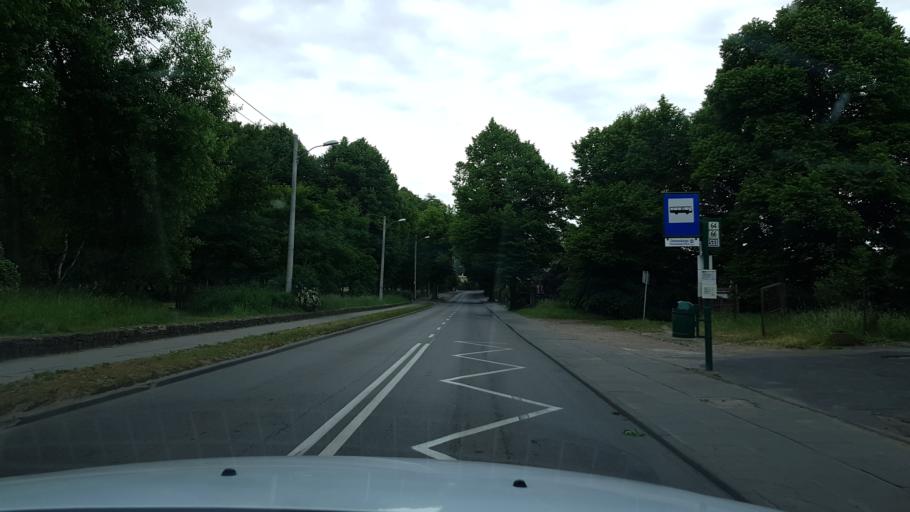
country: PL
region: West Pomeranian Voivodeship
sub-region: Szczecin
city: Szczecin
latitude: 53.3555
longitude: 14.5815
